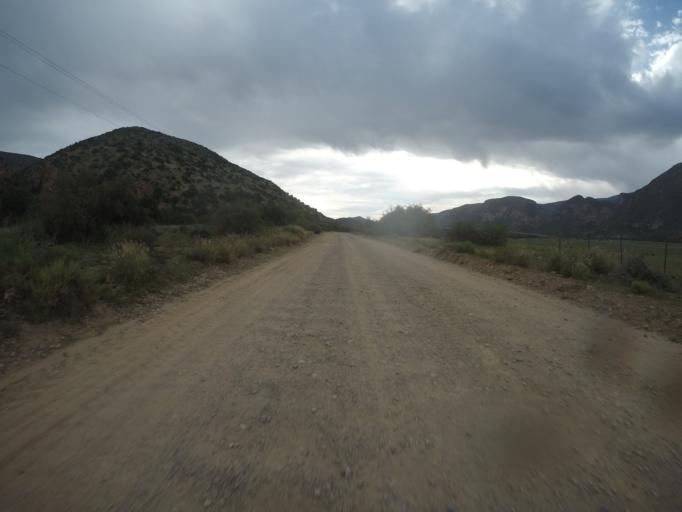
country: ZA
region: Eastern Cape
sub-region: Cacadu District Municipality
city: Willowmore
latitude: -33.5262
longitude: 23.8528
